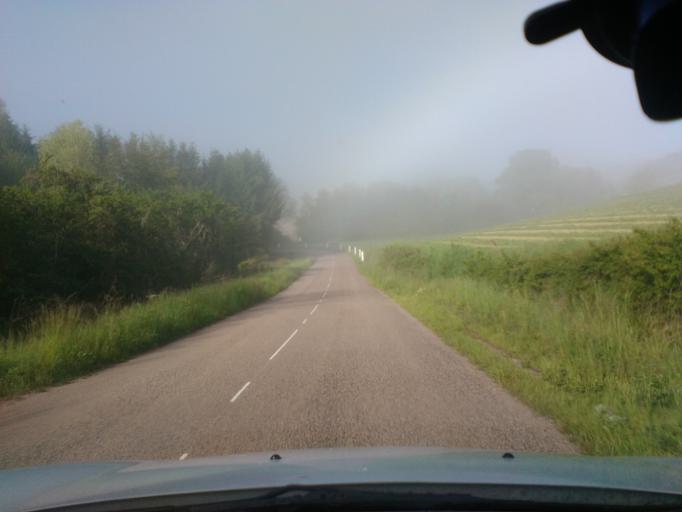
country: FR
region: Lorraine
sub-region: Departement des Vosges
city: Charmes
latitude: 48.3400
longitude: 6.2352
